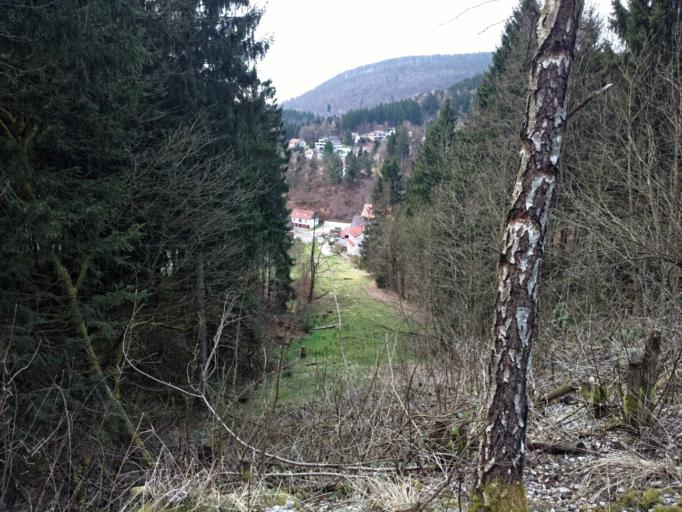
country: DE
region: Lower Saxony
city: Bad Grund
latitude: 51.8051
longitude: 10.2479
